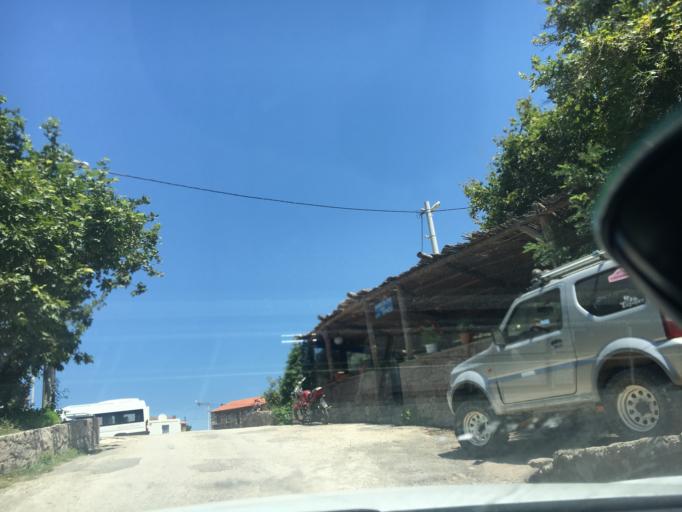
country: TR
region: Canakkale
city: Gulpinar
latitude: 39.4791
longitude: 26.0648
